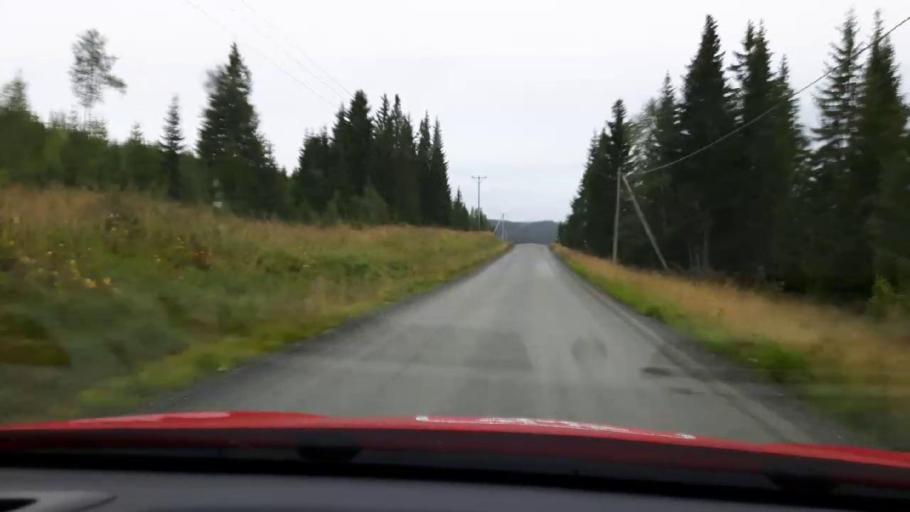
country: SE
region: Jaemtland
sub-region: Are Kommun
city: Are
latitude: 63.4171
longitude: 12.8265
